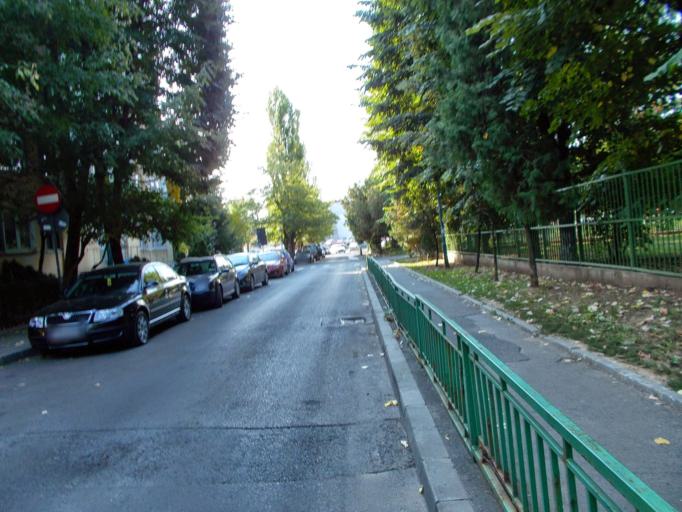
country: RO
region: Ilfov
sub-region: Comuna Popesti-Leordeni
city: Popesti-Leordeni
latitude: 44.3768
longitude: 26.1149
